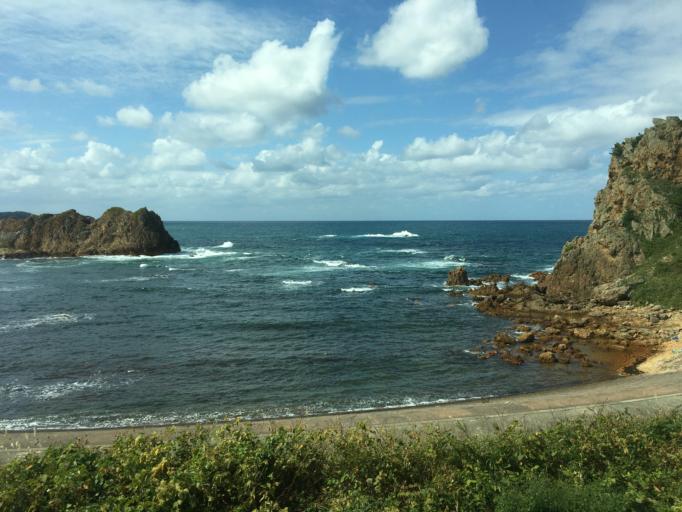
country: JP
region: Aomori
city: Shimokizukuri
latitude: 40.6603
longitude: 139.9381
